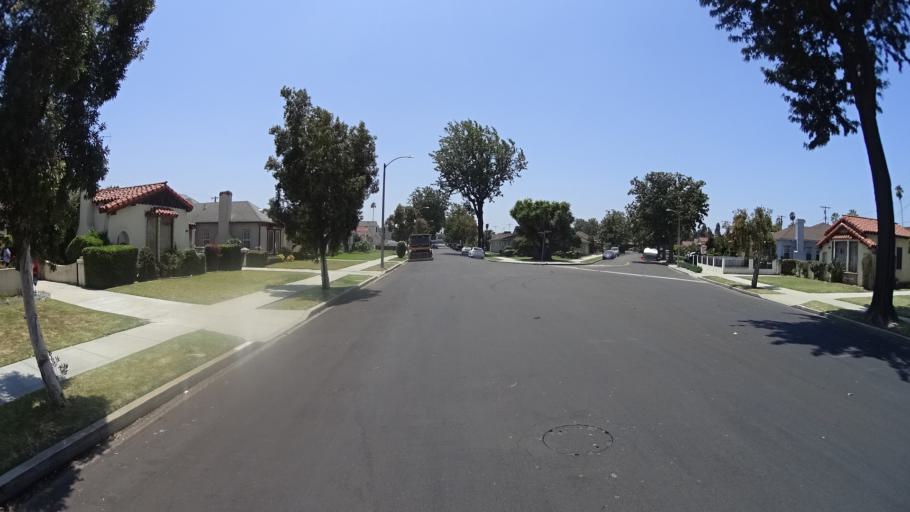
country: US
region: California
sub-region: Los Angeles County
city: View Park-Windsor Hills
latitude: 34.0143
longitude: -118.3281
